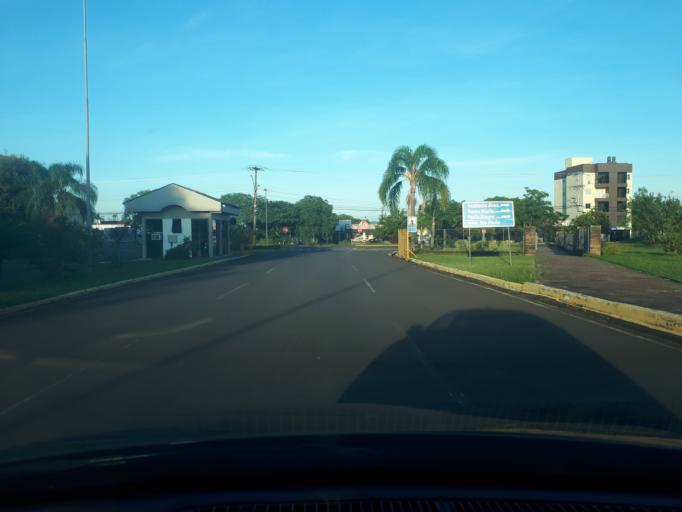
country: BR
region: Rio Grande do Sul
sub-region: Santa Cruz Do Sul
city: Santa Cruz do Sul
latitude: -29.6985
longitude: -52.4412
